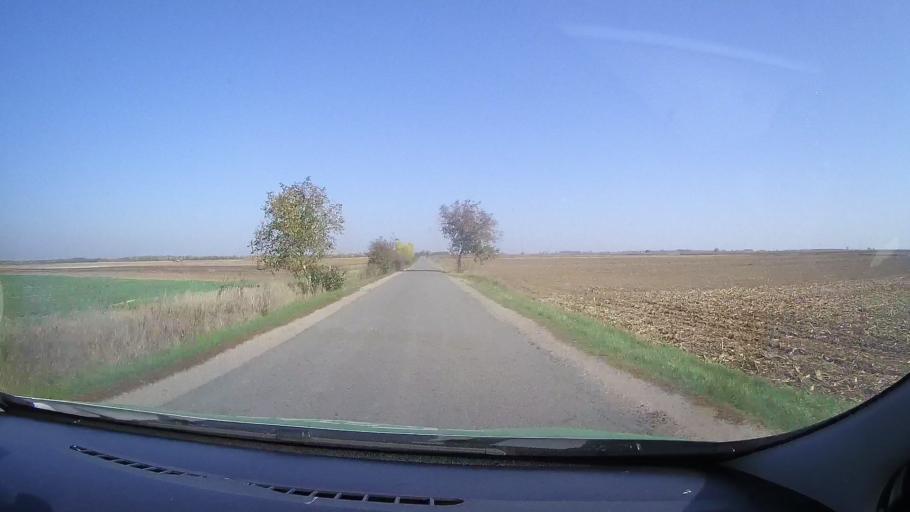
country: RO
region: Satu Mare
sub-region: Comuna Ciumesti
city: Ciumesti
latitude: 47.6735
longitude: 22.3431
